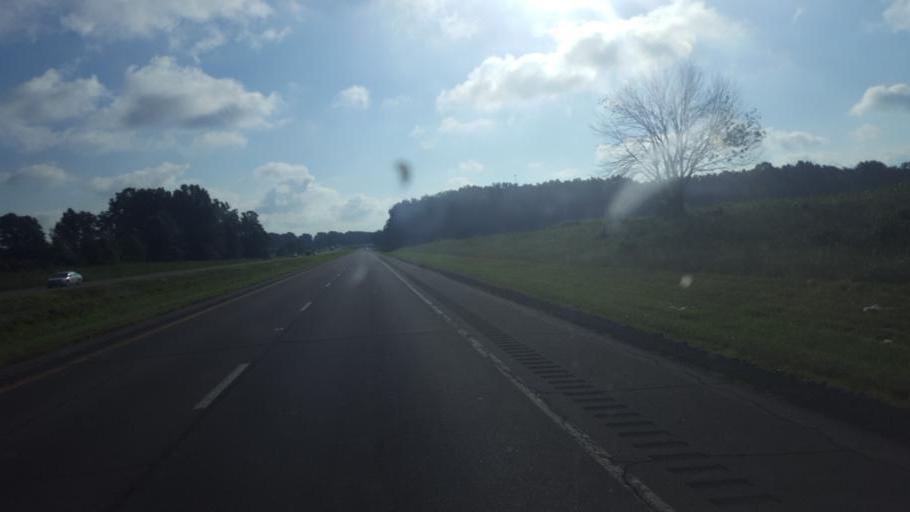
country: US
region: Ohio
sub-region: Wayne County
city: Wooster
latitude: 40.7965
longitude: -82.0445
